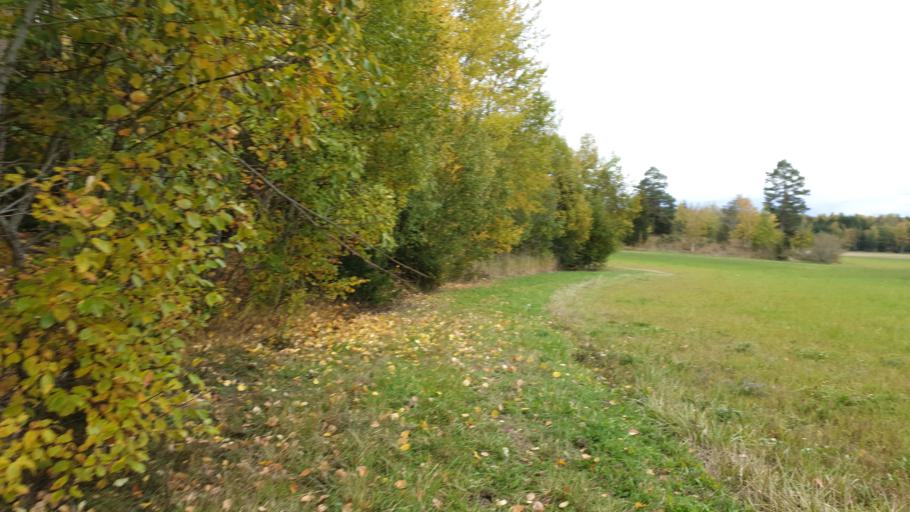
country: SE
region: Vaestmanland
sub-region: Sala Kommun
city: Sala
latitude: 59.8159
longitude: 16.6496
